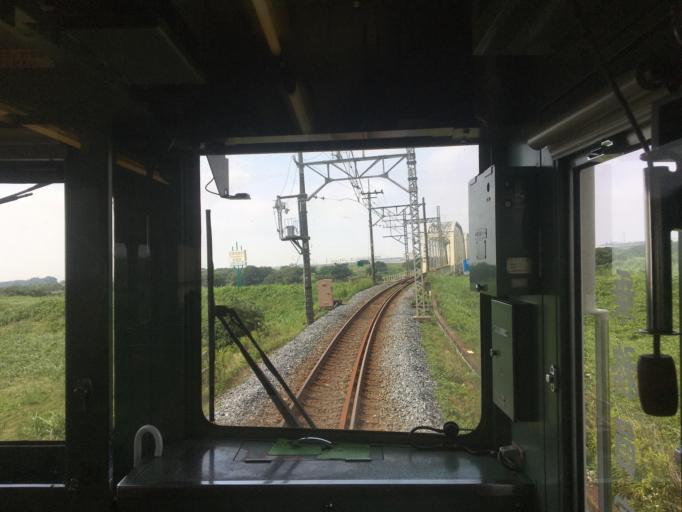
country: JP
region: Gunma
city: Tatebayashi
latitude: 36.2737
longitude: 139.5571
